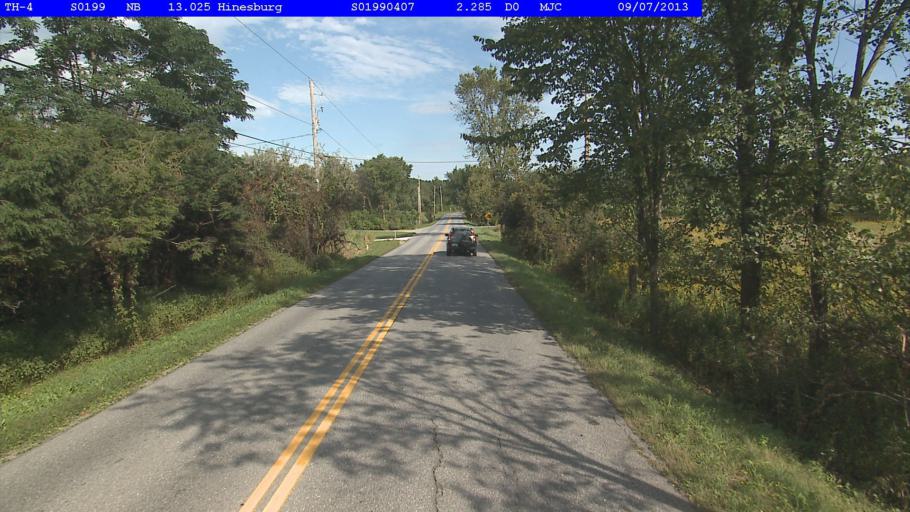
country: US
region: Vermont
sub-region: Chittenden County
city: Hinesburg
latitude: 44.3107
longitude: -73.1099
